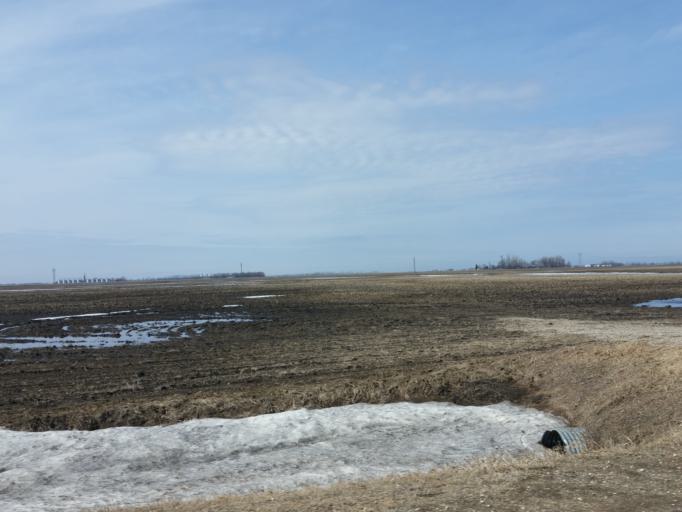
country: US
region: North Dakota
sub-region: Walsh County
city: Grafton
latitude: 48.2989
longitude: -97.2549
